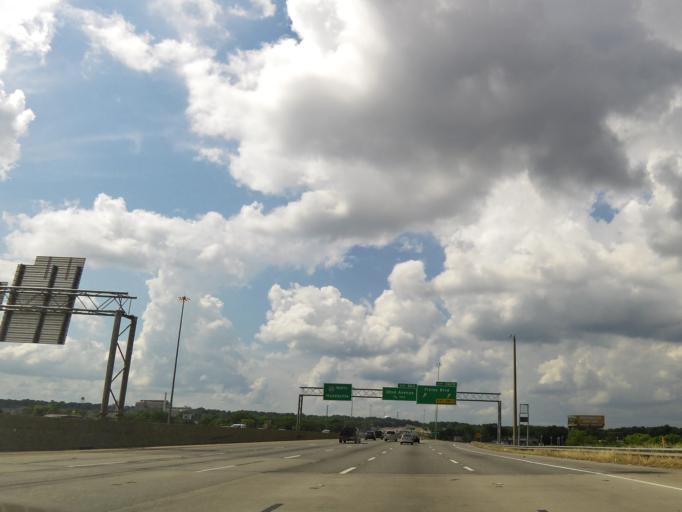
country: US
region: Alabama
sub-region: Jefferson County
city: Birmingham
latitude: 33.5389
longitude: -86.8245
